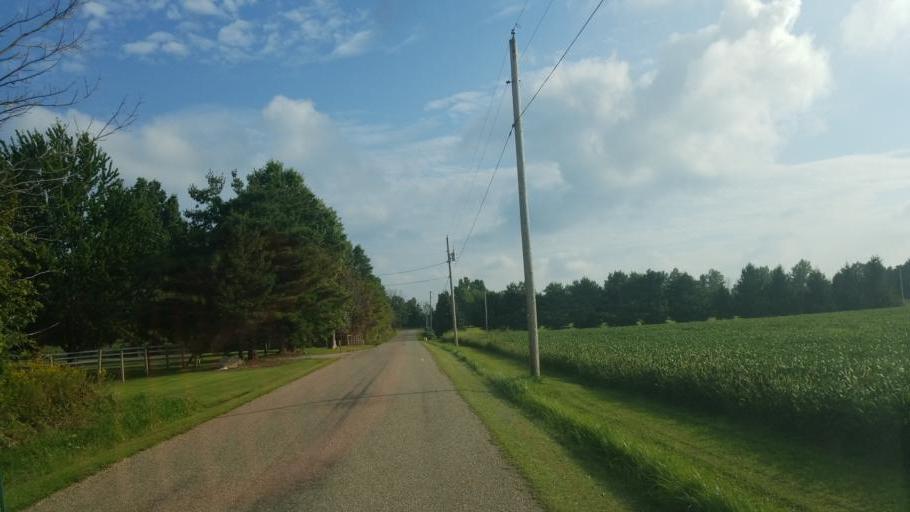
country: US
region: Ohio
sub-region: Medina County
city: Lodi
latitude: 40.9556
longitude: -82.0042
